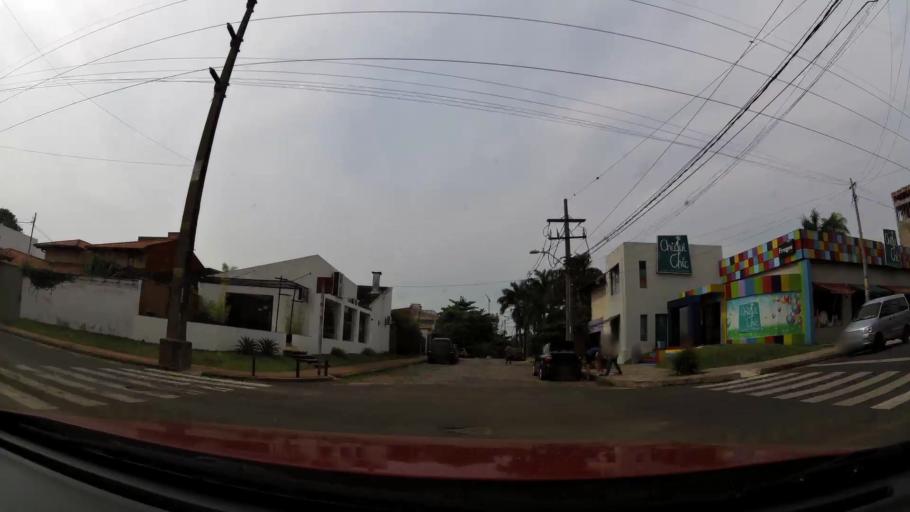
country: PY
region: Central
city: Fernando de la Mora
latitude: -25.2903
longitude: -57.5611
